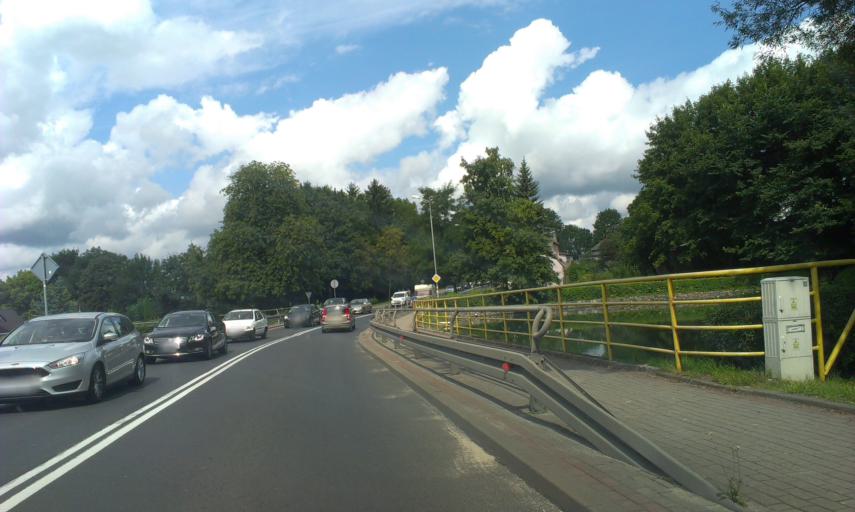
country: PL
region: West Pomeranian Voivodeship
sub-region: Powiat koszalinski
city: Bobolice
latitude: 53.9556
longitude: 16.5864
